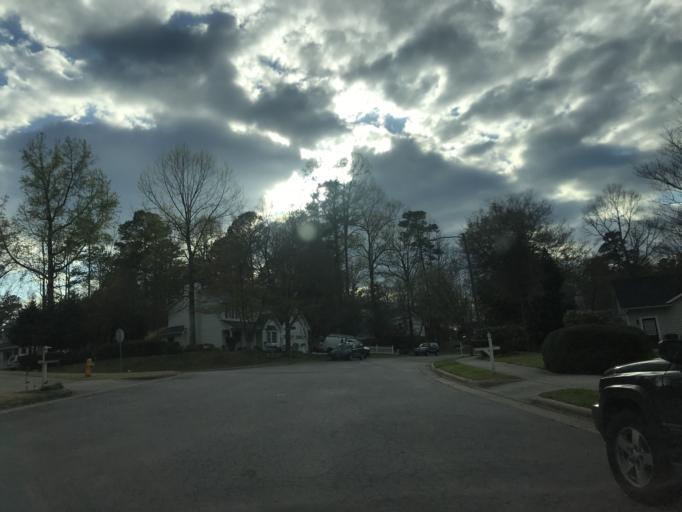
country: US
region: North Carolina
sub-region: Wake County
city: Knightdale
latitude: 35.8653
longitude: -78.5611
